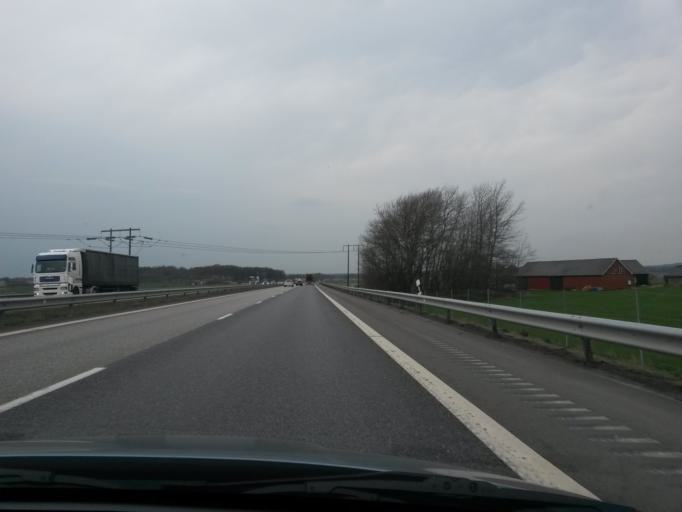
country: SE
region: Halland
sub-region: Varbergs Kommun
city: Traslovslage
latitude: 57.1007
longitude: 12.3380
